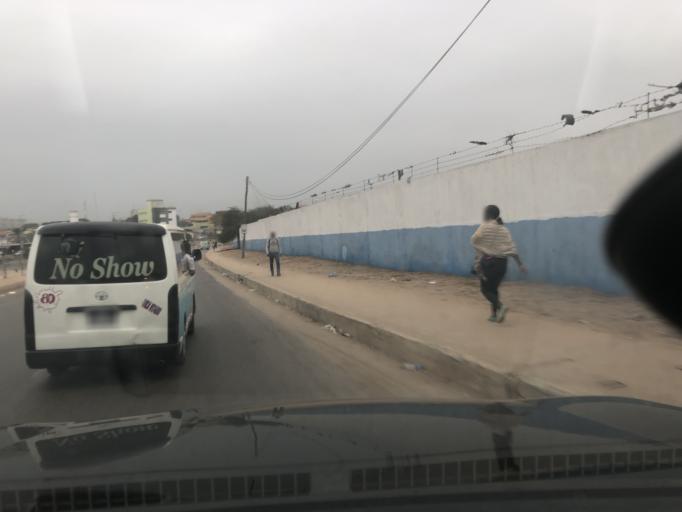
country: AO
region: Luanda
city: Luanda
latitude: -8.8526
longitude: 13.2216
